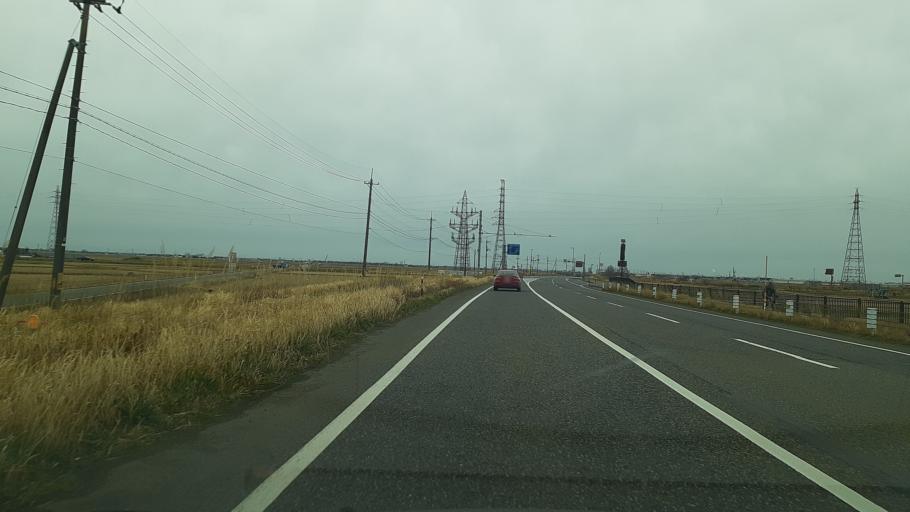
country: JP
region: Niigata
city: Niitsu-honcho
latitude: 37.8009
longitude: 139.1037
